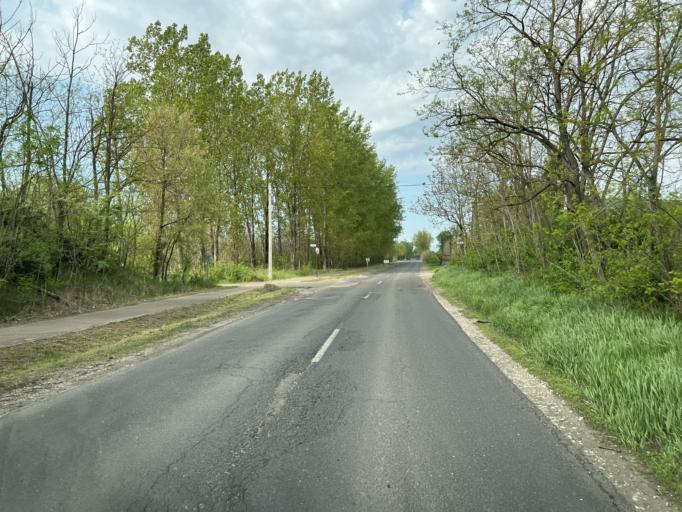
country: HU
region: Pest
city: Farmos
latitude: 47.3797
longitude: 19.8796
